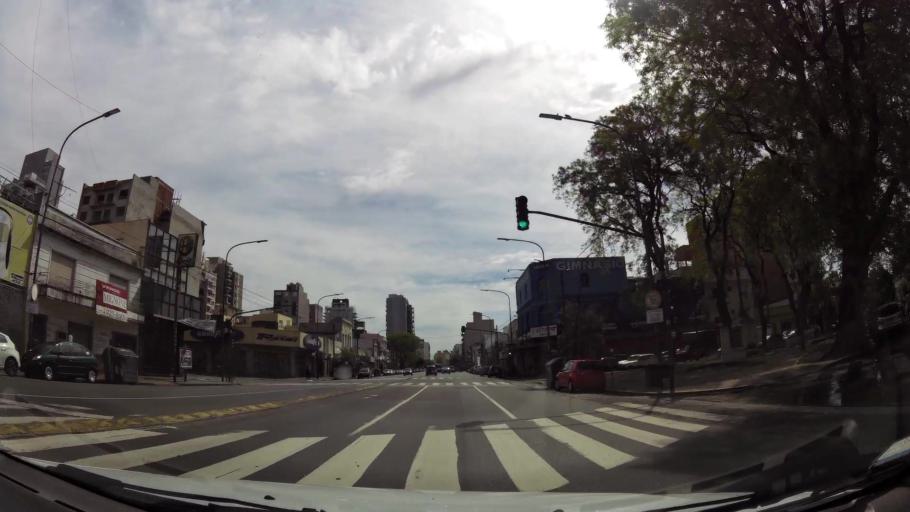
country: AR
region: Buenos Aires F.D.
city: Villa Santa Rita
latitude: -34.6381
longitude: -58.5042
